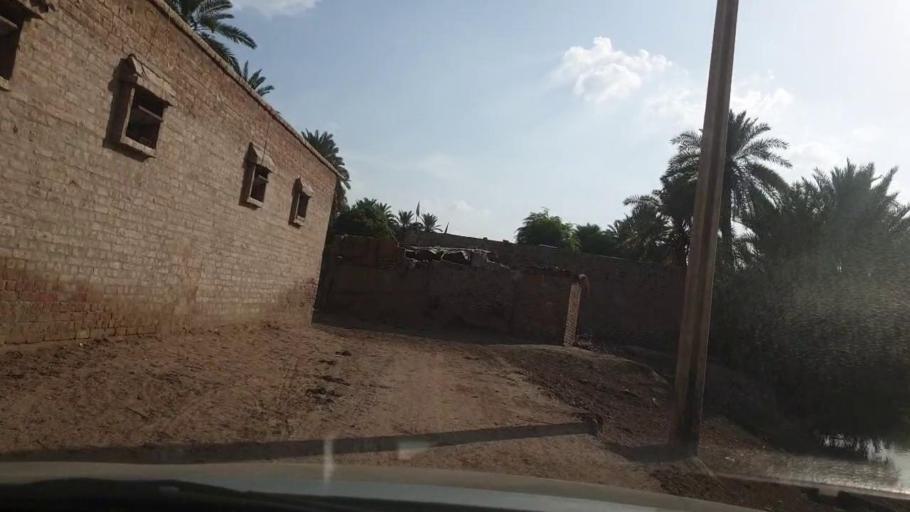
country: PK
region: Sindh
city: Sukkur
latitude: 27.6595
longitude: 68.8307
